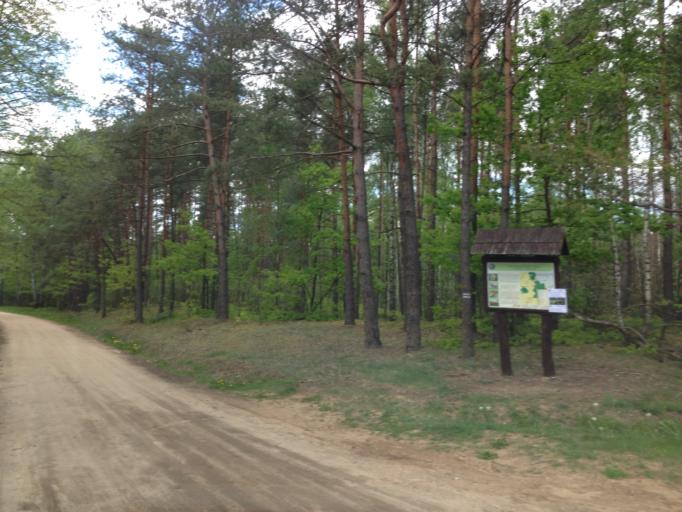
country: PL
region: Podlasie
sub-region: Powiat moniecki
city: Goniadz
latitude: 53.3514
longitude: 22.5980
